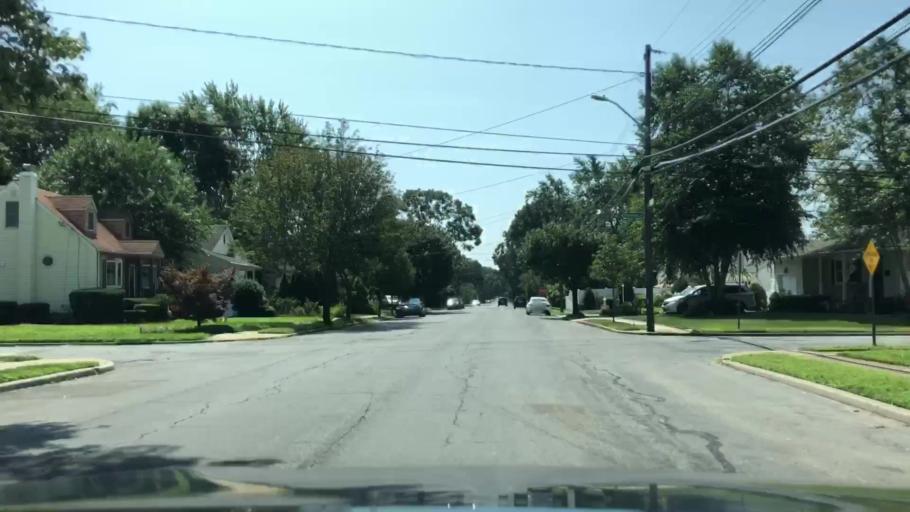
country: US
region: New York
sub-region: Nassau County
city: Massapequa
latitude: 40.6909
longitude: -73.4701
